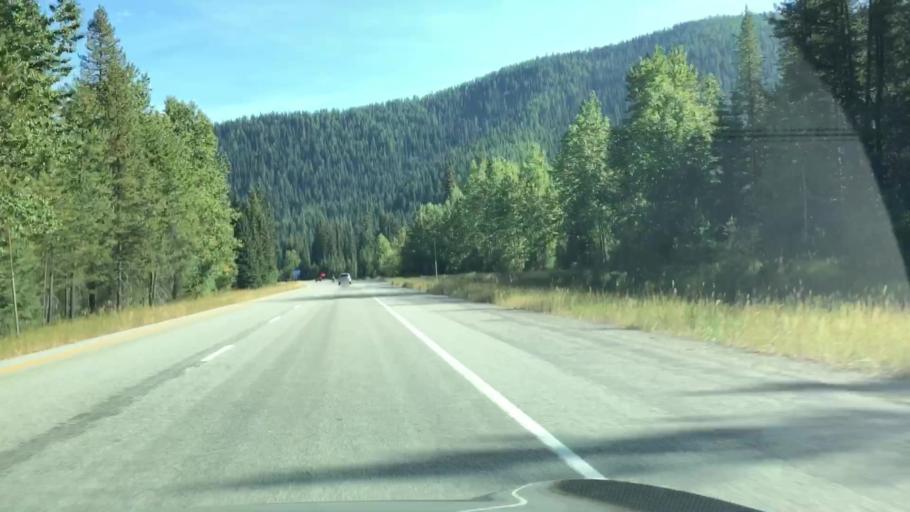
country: US
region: Idaho
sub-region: Shoshone County
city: Wallace
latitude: 47.4267
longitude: -115.6389
